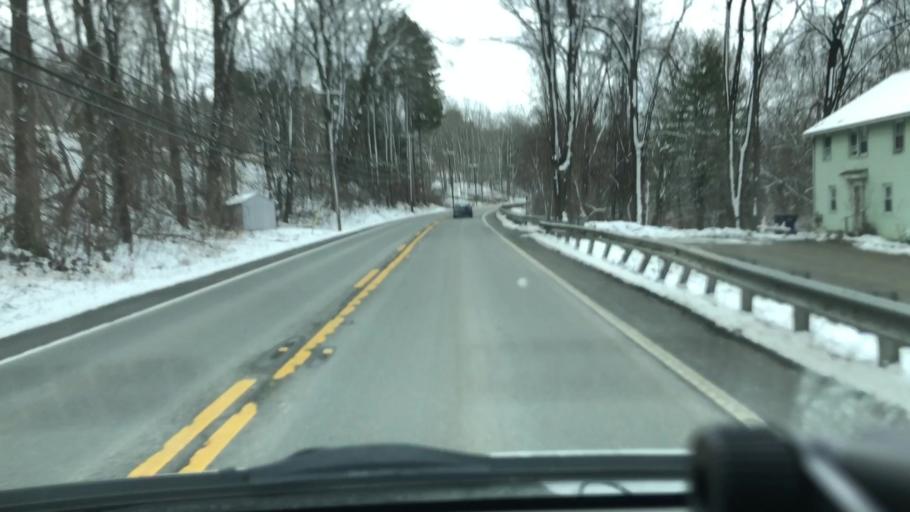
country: US
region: Massachusetts
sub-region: Franklin County
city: Greenfield
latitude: 42.5643
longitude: -72.5931
